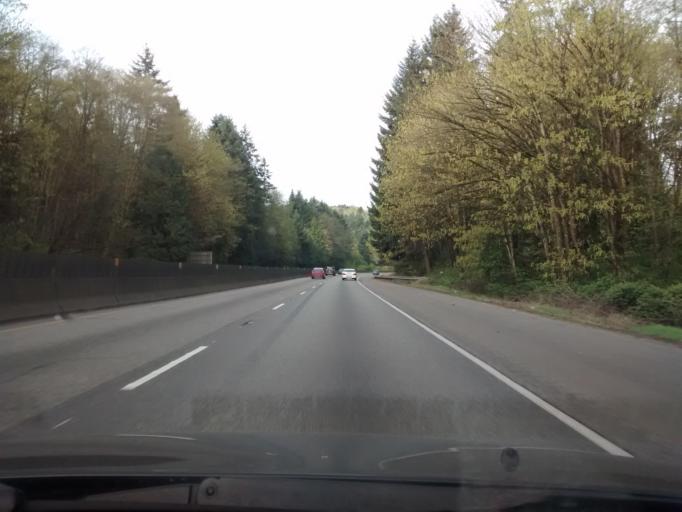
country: US
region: Washington
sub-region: Kitsap County
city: Navy Yard City
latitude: 47.5288
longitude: -122.6730
